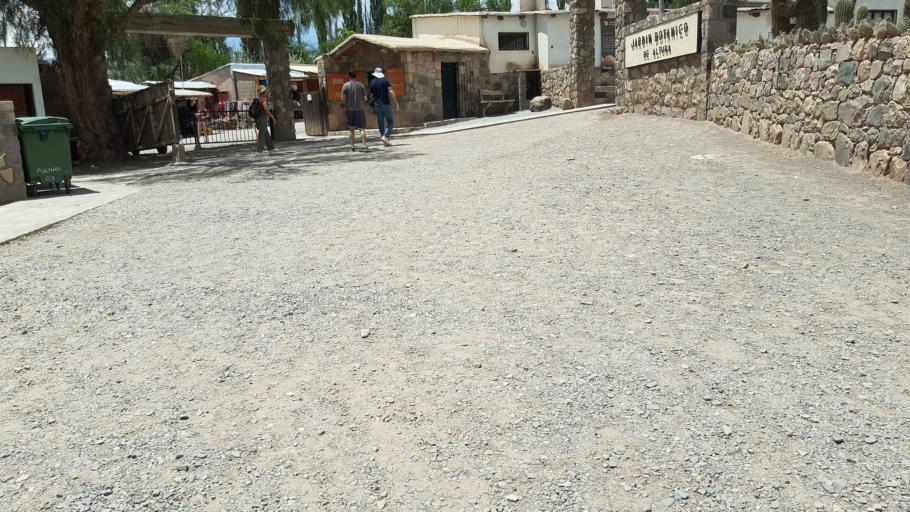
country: AR
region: Jujuy
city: Maimara
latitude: -23.5842
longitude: -65.4001
